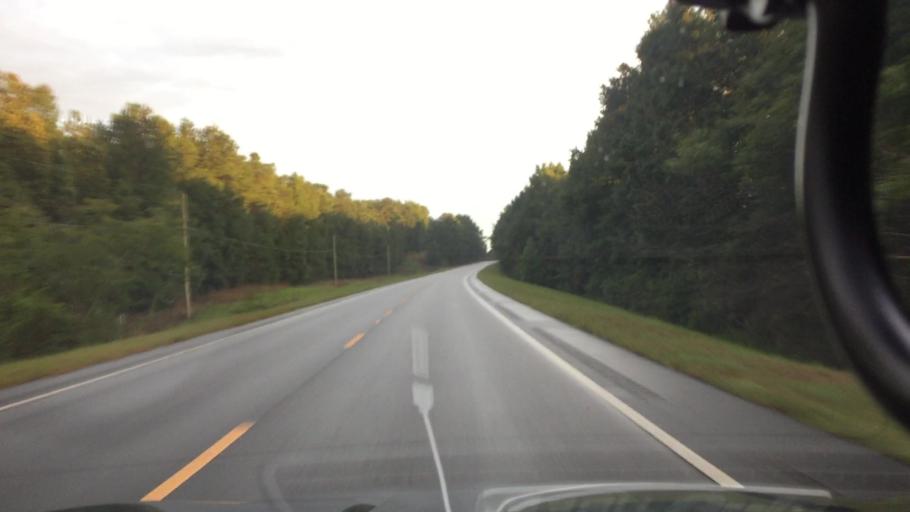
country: US
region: Alabama
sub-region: Coffee County
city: New Brockton
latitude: 31.5540
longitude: -85.9210
